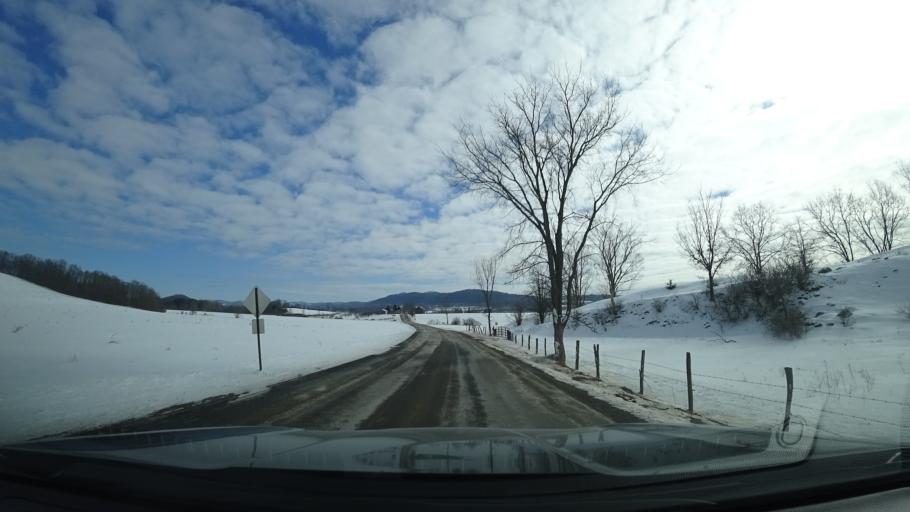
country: US
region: New York
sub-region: Washington County
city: Fort Edward
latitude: 43.2518
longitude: -73.4857
